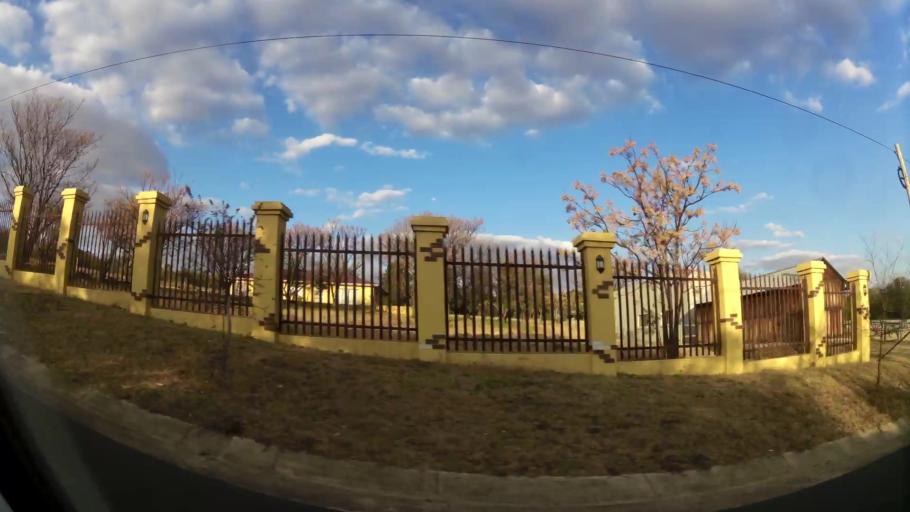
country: ZA
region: Gauteng
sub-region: City of Johannesburg Metropolitan Municipality
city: Diepsloot
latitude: -25.9981
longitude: 27.9682
